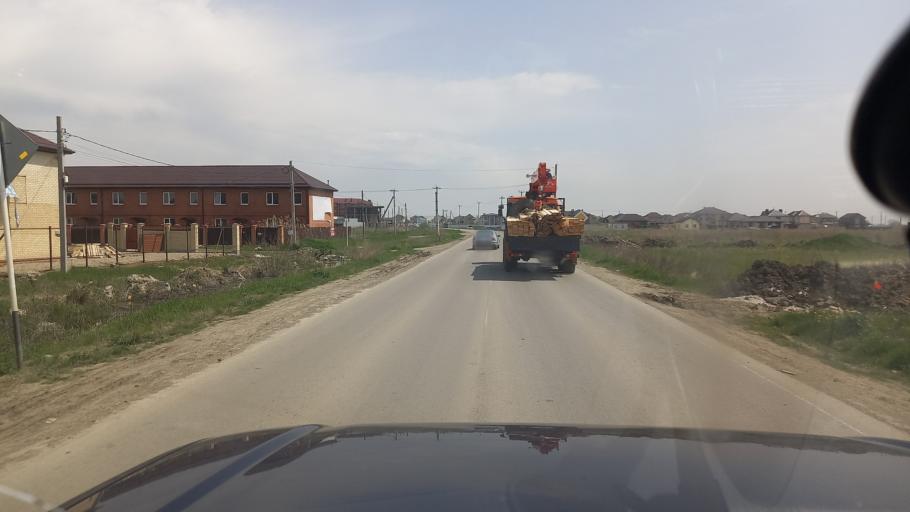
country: RU
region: Adygeya
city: Yablonovskiy
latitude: 44.9854
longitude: 38.9696
